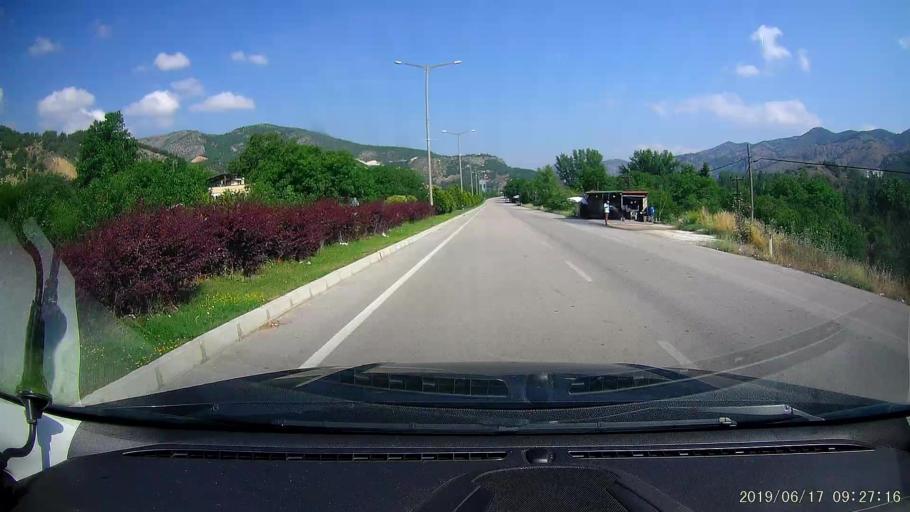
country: TR
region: Amasya
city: Amasya
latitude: 40.6754
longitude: 35.8279
